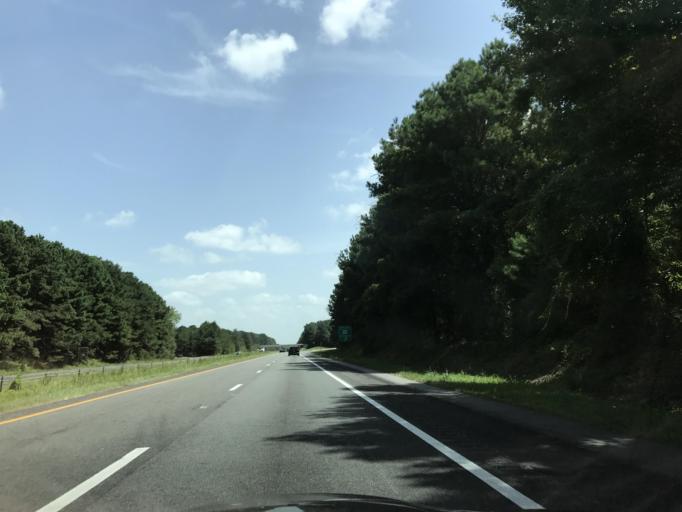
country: US
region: North Carolina
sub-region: Sampson County
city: Plain View
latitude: 35.2289
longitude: -78.3557
